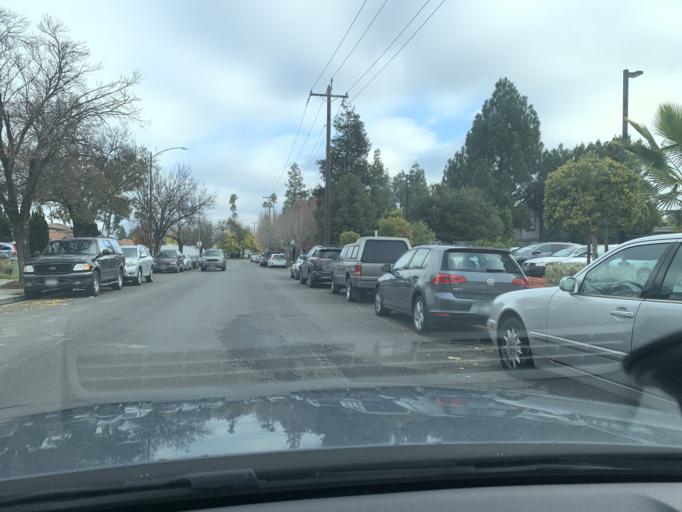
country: US
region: California
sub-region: Santa Clara County
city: San Jose
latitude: 37.3292
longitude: -121.8561
